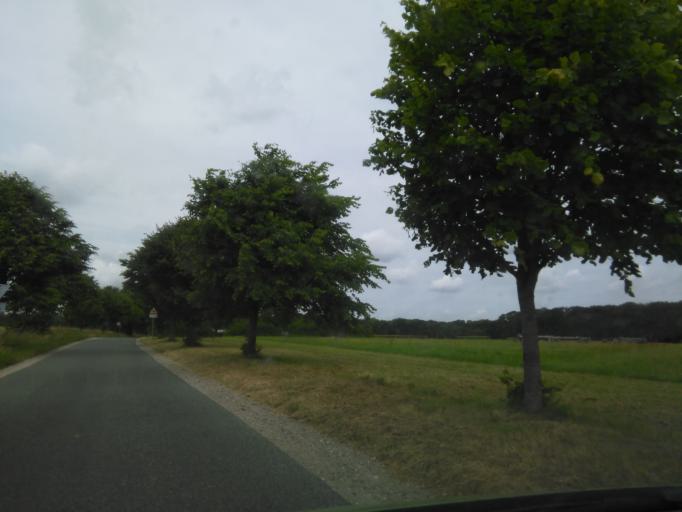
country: DK
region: Central Jutland
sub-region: Arhus Kommune
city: Beder
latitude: 56.0633
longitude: 10.1953
